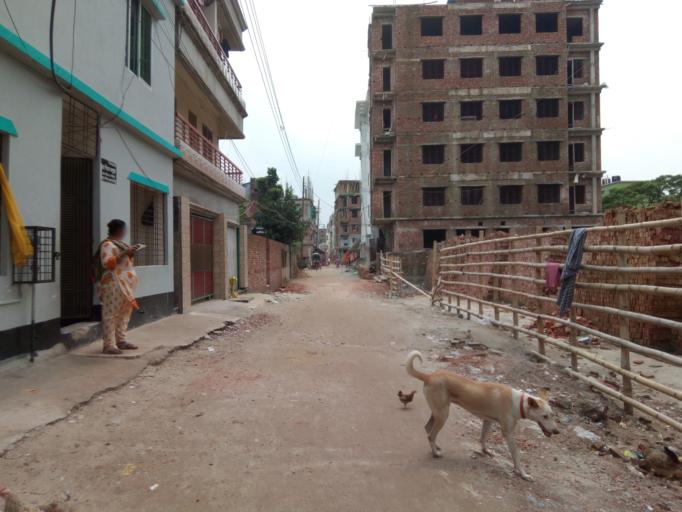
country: BD
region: Dhaka
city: Azimpur
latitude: 23.7554
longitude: 90.3529
